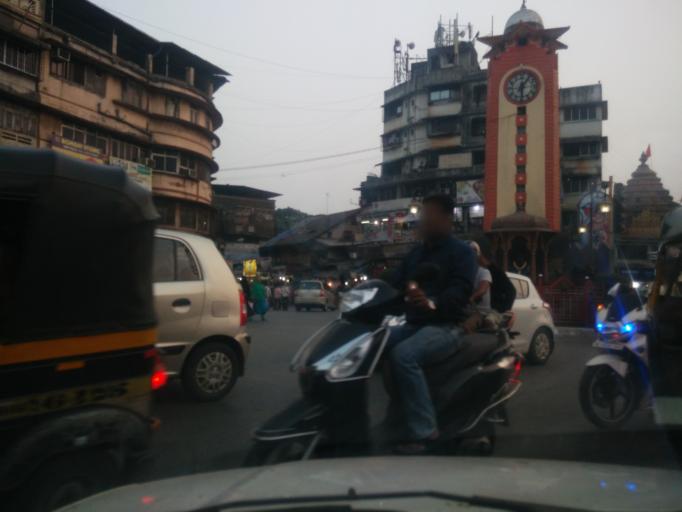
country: IN
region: Maharashtra
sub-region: Thane
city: Kalyan
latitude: 19.2402
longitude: 73.1292
